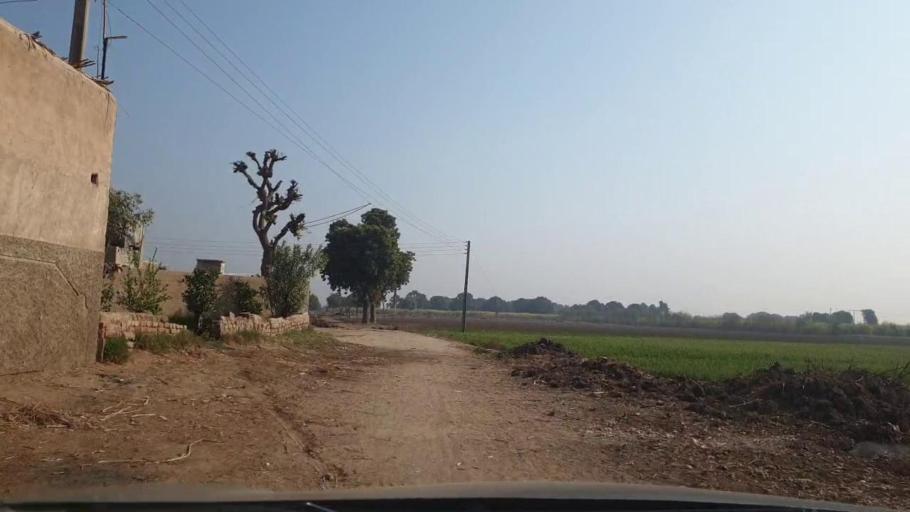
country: PK
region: Sindh
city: Tando Allahyar
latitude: 25.4842
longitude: 68.7447
